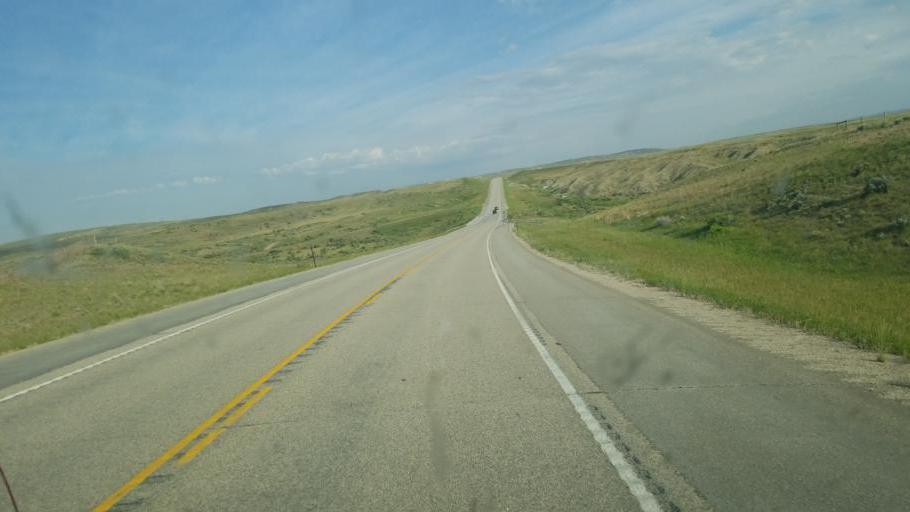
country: US
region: Wyoming
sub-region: Natrona County
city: Mills
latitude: 43.0340
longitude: -107.0160
